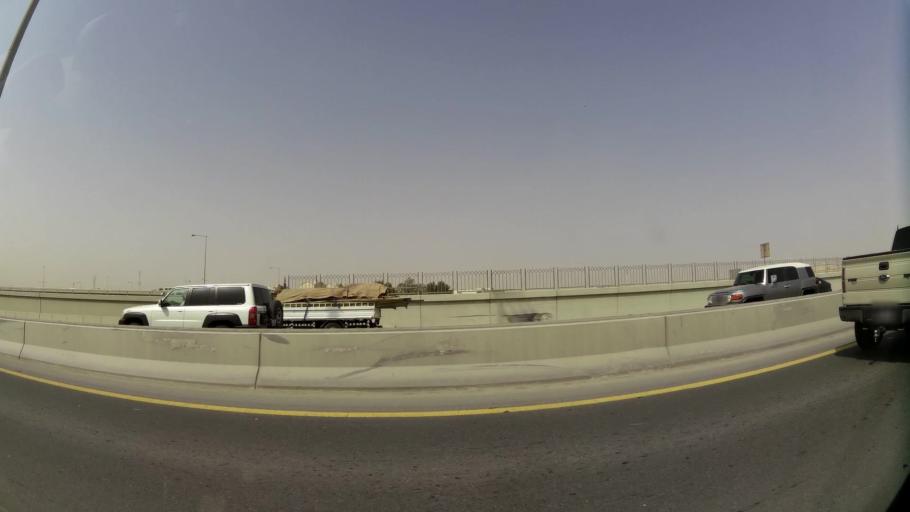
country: QA
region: Baladiyat ar Rayyan
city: Ar Rayyan
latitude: 25.2991
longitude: 51.4746
